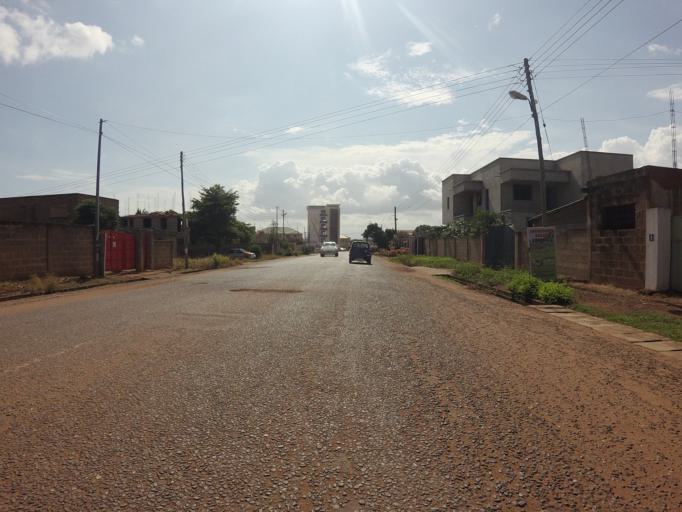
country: GH
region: Greater Accra
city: Medina Estates
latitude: 5.6688
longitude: -0.1869
